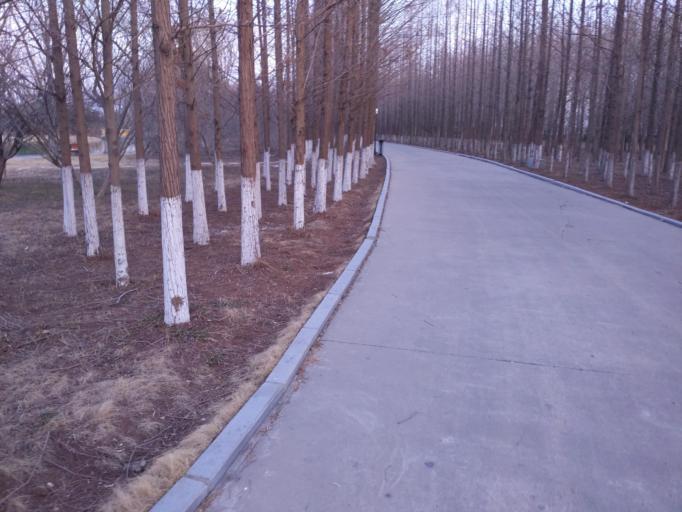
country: CN
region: Henan Sheng
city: Puyang
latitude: 35.7771
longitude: 114.9445
